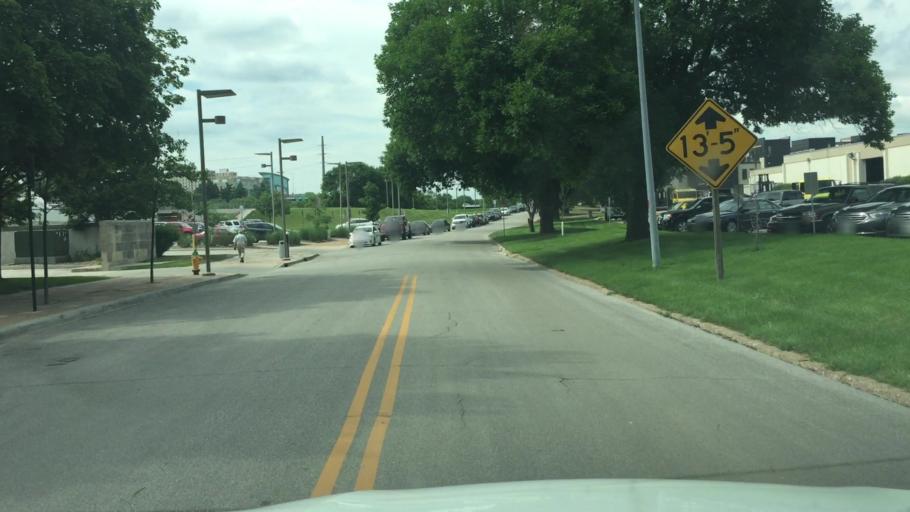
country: US
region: Iowa
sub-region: Polk County
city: Des Moines
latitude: 41.5909
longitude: -93.6170
